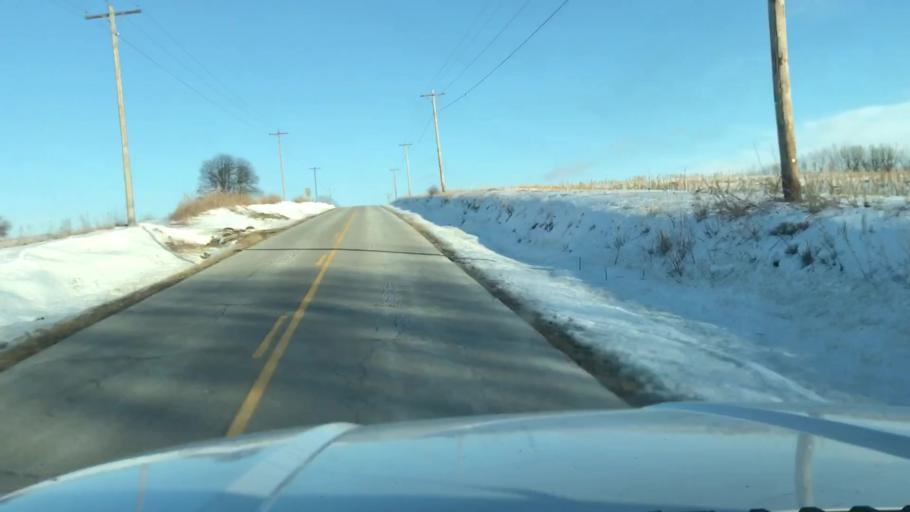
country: US
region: Missouri
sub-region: Andrew County
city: Savannah
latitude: 40.0247
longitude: -94.8894
